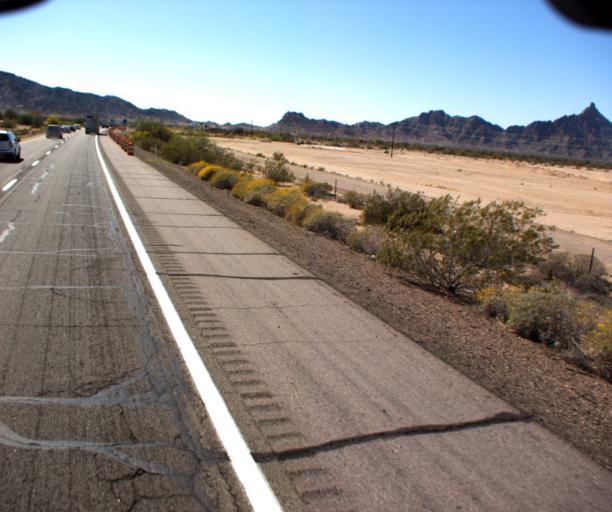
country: US
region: Arizona
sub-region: Yuma County
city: Wellton
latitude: 32.7328
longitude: -113.7096
